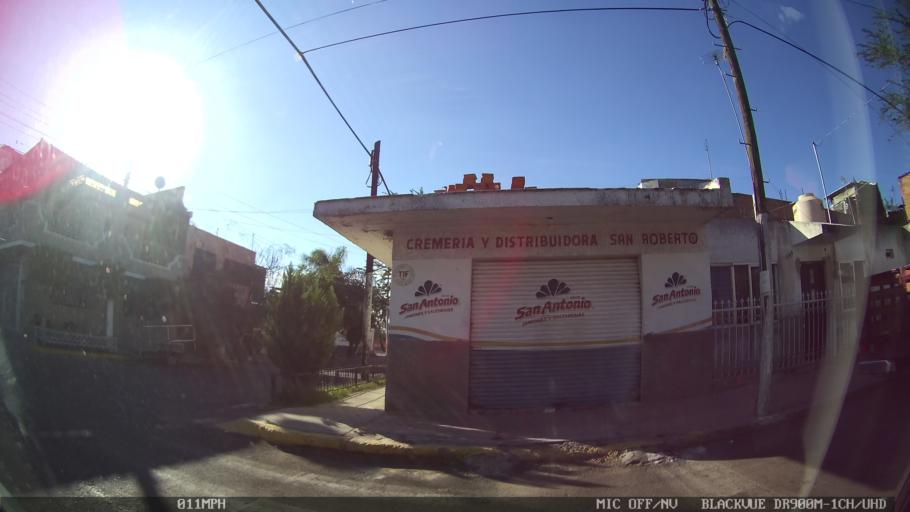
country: MX
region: Jalisco
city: Tlaquepaque
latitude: 20.7117
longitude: -103.2937
